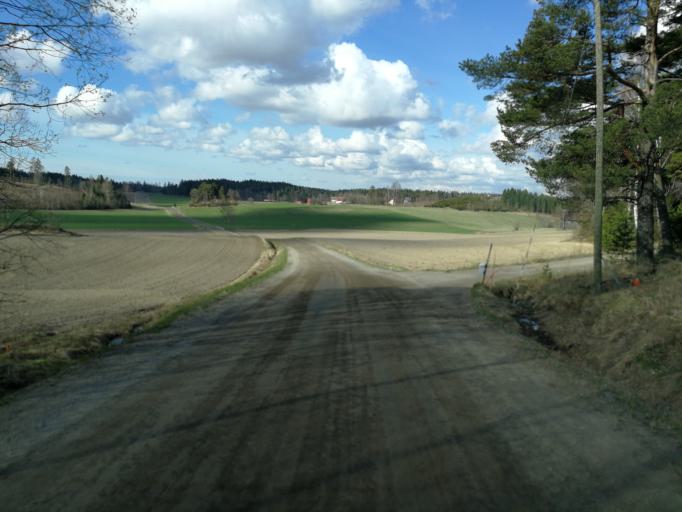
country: FI
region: Uusimaa
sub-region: Raaseporin
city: Inga
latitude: 60.1346
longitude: 24.0647
